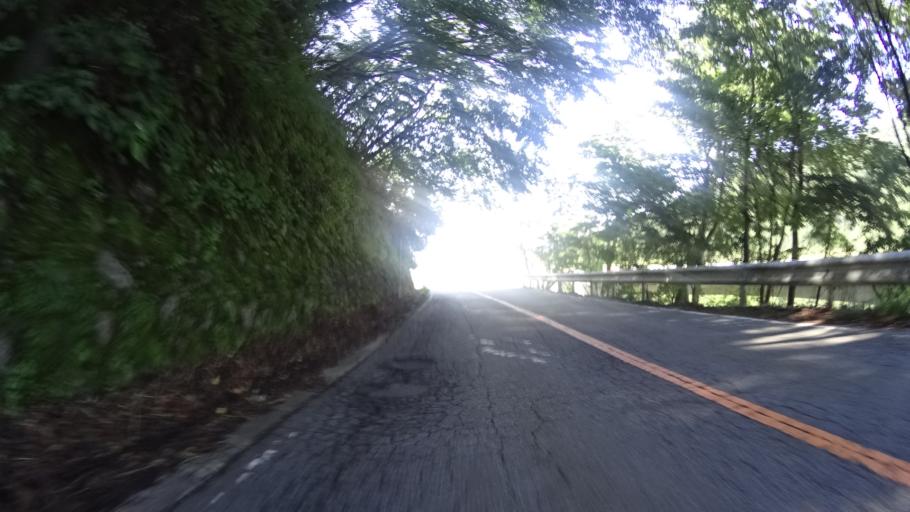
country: JP
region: Yamanashi
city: Enzan
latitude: 35.7697
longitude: 138.8053
